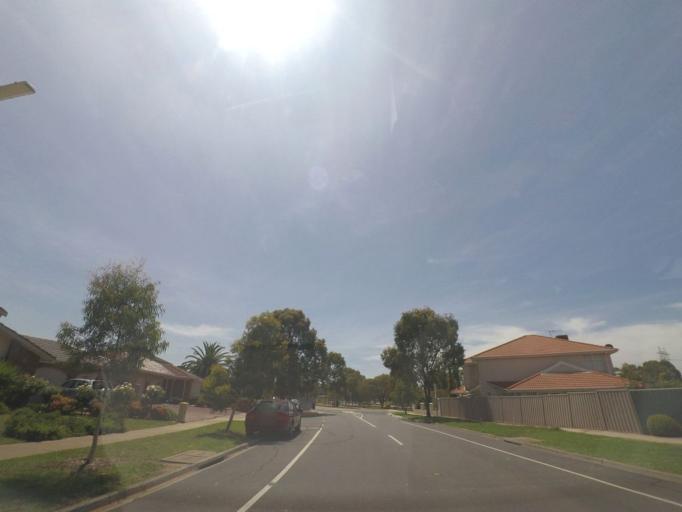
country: AU
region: Victoria
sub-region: Brimbank
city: Keilor Lodge
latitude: -37.7053
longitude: 144.7947
